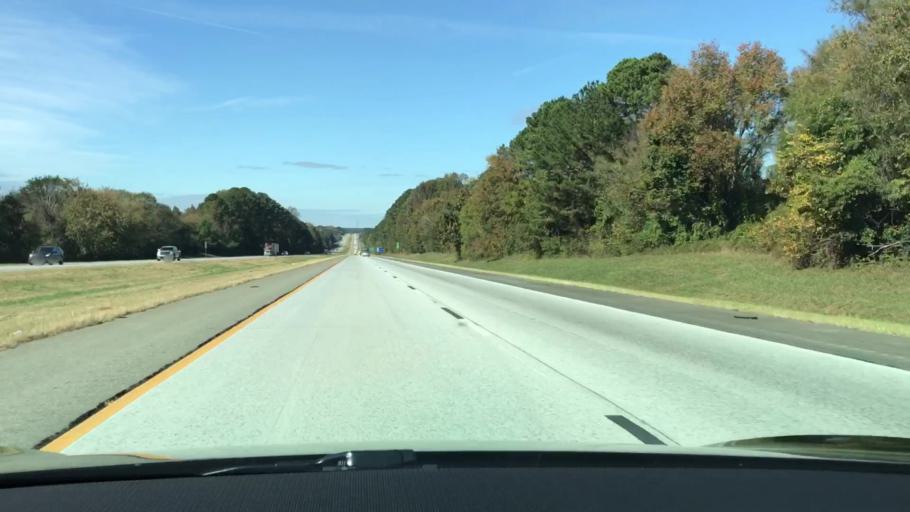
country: US
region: Georgia
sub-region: Putnam County
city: Jefferson
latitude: 33.5431
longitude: -83.3263
